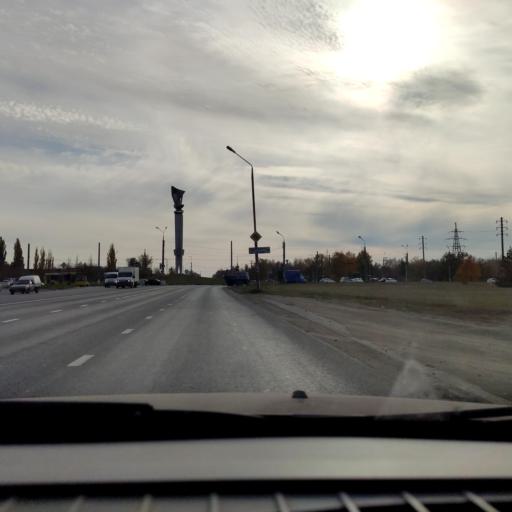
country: RU
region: Samara
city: Tol'yatti
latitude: 53.5549
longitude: 49.2879
